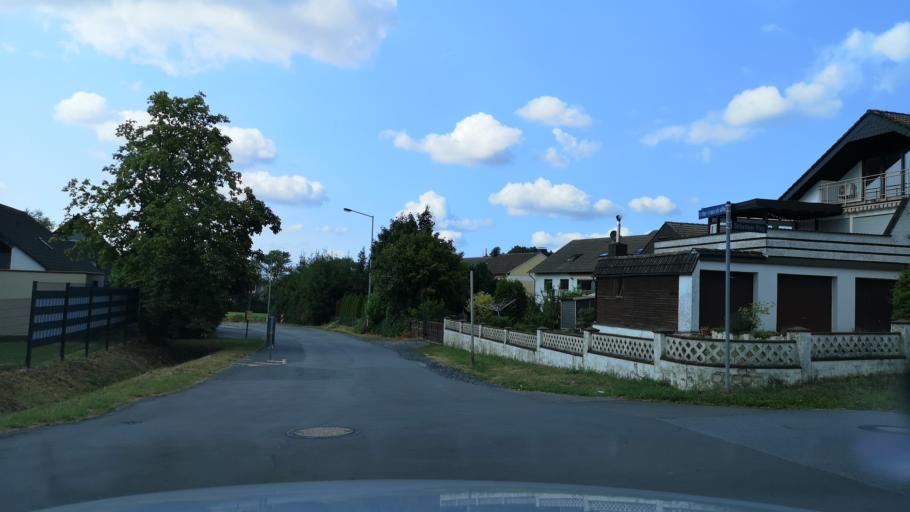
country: DE
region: North Rhine-Westphalia
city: Iserlohn
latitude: 51.4262
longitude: 7.7146
